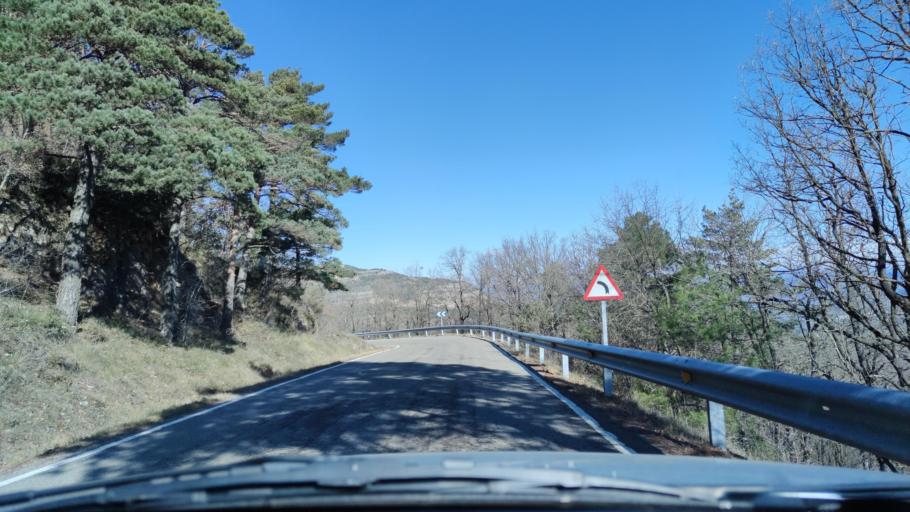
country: ES
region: Catalonia
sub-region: Provincia de Lleida
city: Llimiana
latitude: 42.0456
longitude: 1.0648
